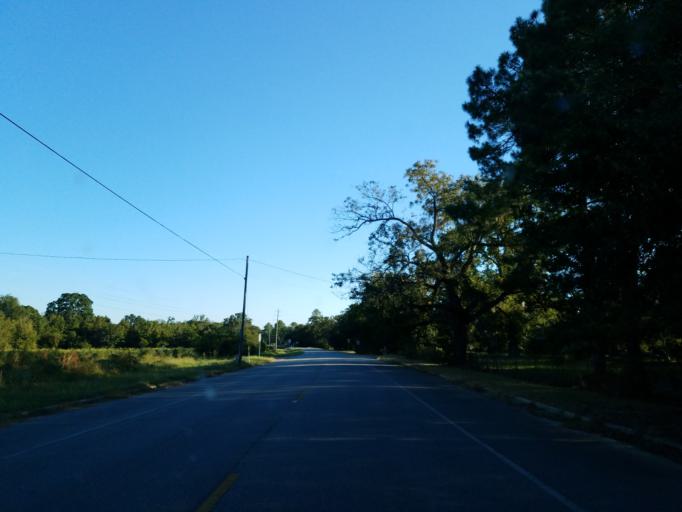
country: US
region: Georgia
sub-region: Worth County
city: Sylvester
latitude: 31.6984
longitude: -83.8855
